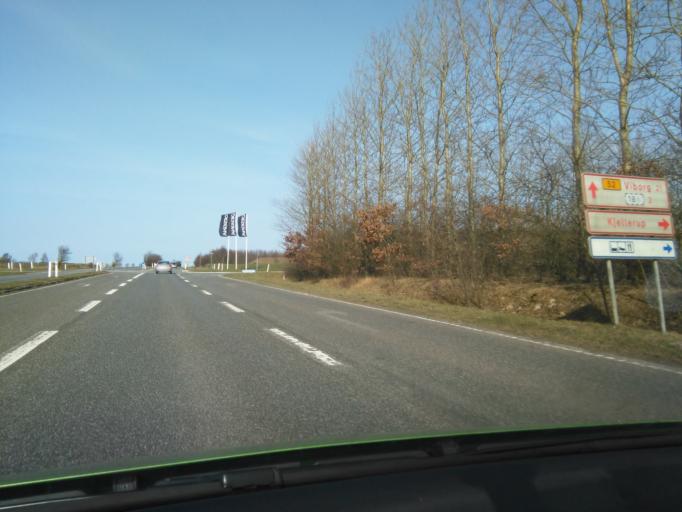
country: DK
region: Central Jutland
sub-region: Silkeborg Kommune
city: Kjellerup
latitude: 56.2749
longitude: 9.4173
